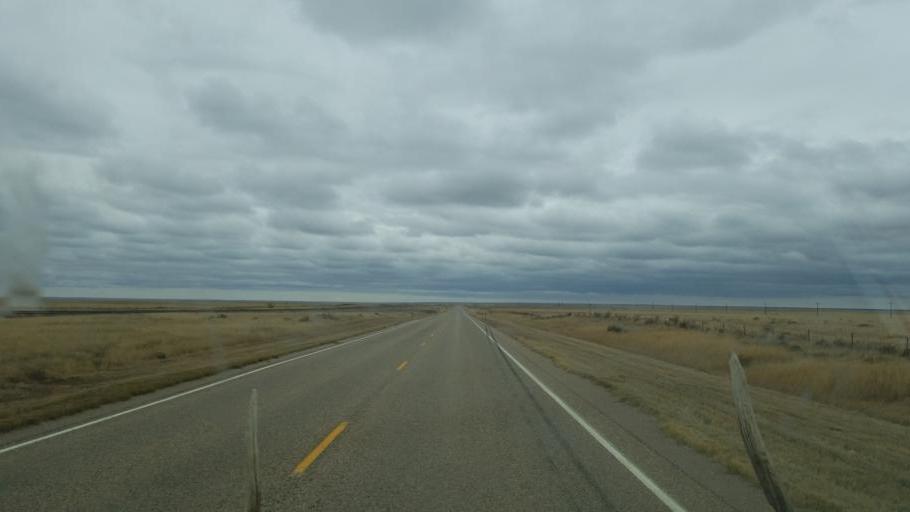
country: US
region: Colorado
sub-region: Kiowa County
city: Eads
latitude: 38.7667
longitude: -102.7713
